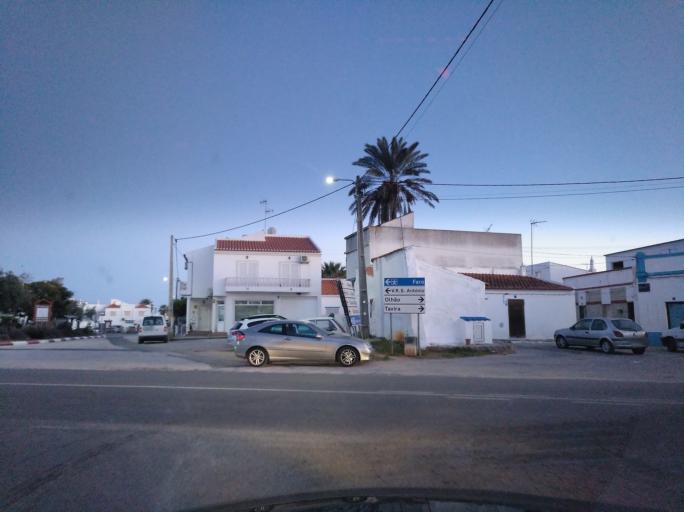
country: PT
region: Faro
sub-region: Vila Real de Santo Antonio
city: Monte Gordo
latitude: 37.1808
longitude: -7.5036
